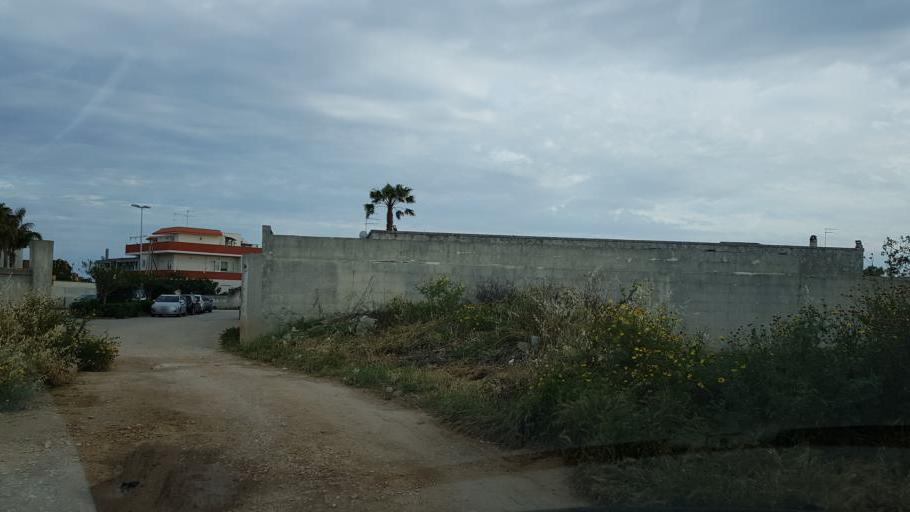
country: IT
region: Apulia
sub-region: Provincia di Brindisi
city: Materdomini
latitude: 40.6557
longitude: 17.9539
